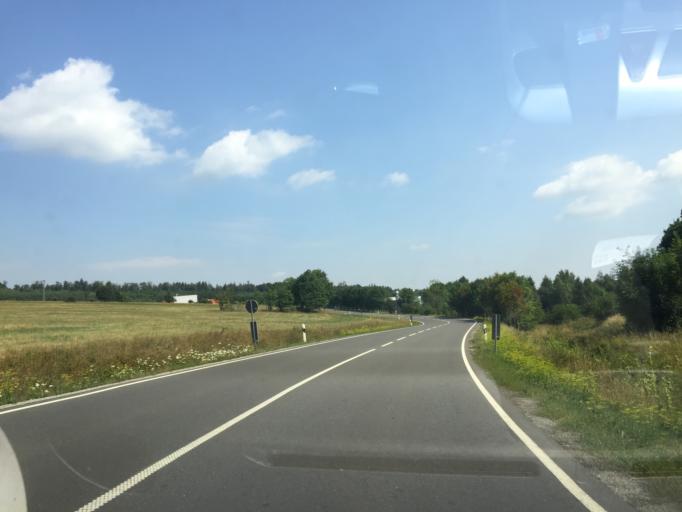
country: DE
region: Saxony-Anhalt
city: Elbingerode
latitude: 51.7640
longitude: 10.7846
